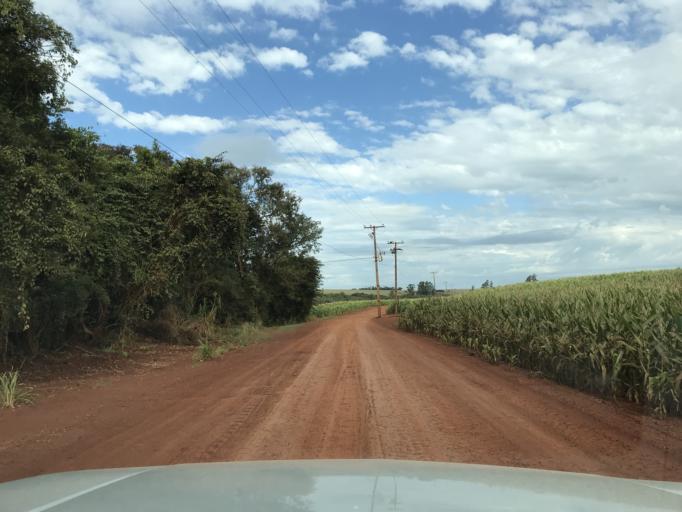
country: BR
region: Parana
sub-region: Palotina
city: Palotina
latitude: -24.3147
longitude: -53.8073
